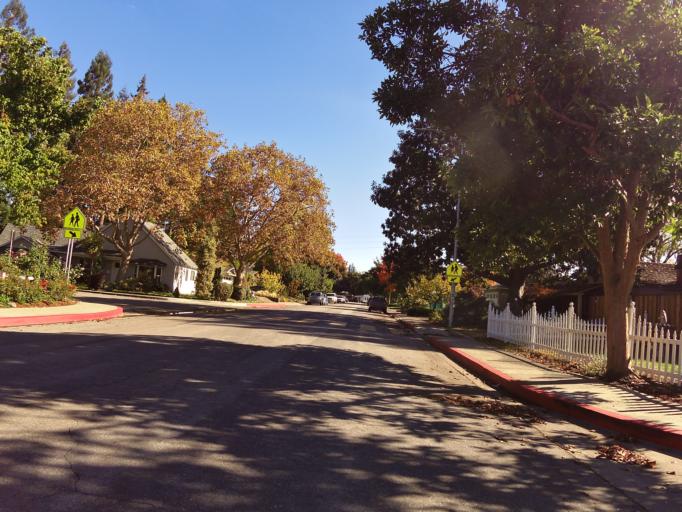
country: US
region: California
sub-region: Santa Clara County
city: Mountain View
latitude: 37.3869
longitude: -122.0722
